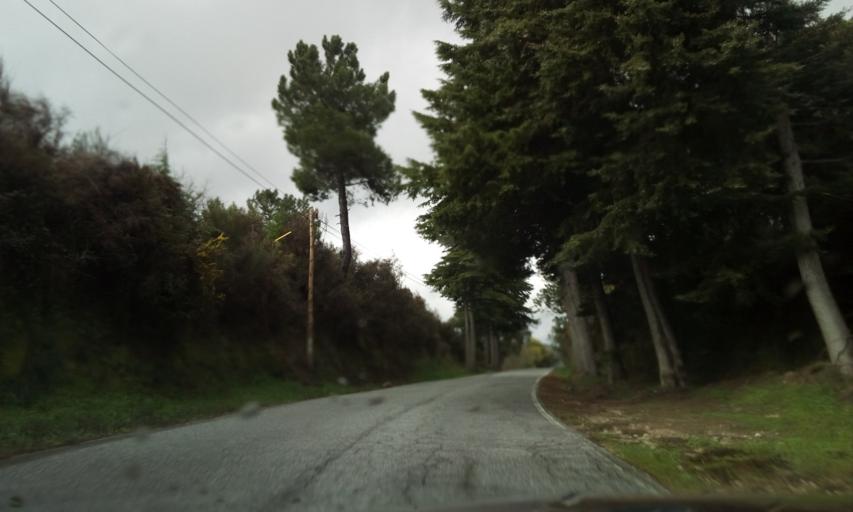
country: PT
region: Guarda
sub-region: Fornos de Algodres
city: Fornos de Algodres
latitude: 40.6078
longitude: -7.5830
